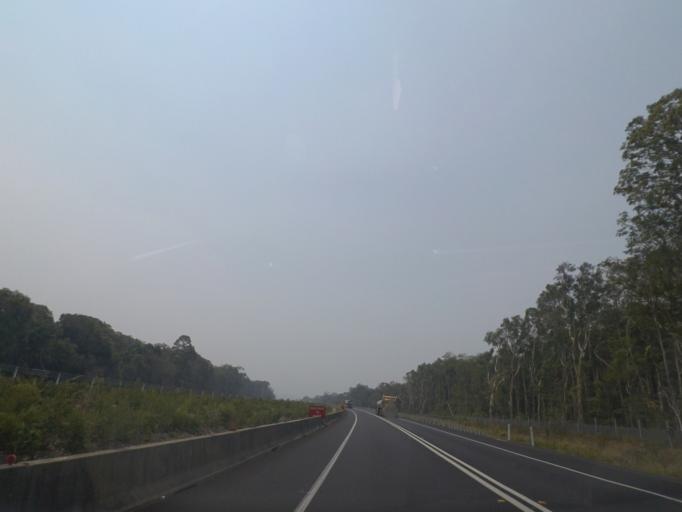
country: AU
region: New South Wales
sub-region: Ballina
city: Ballina
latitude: -28.9144
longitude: 153.4781
